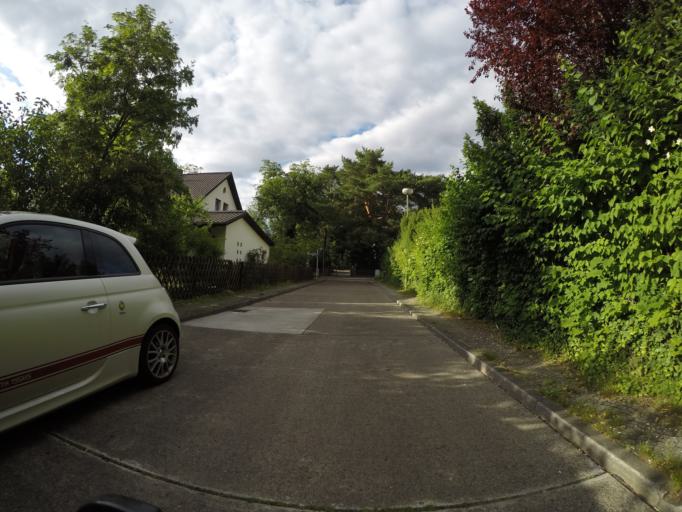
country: DE
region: Berlin
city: Grunewald
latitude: 52.4845
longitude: 13.2727
